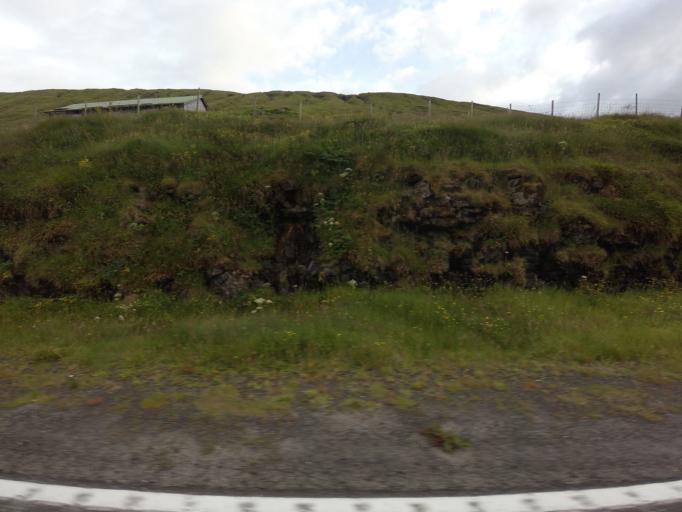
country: FO
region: Streymoy
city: Kollafjordhur
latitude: 62.1696
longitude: -6.9650
